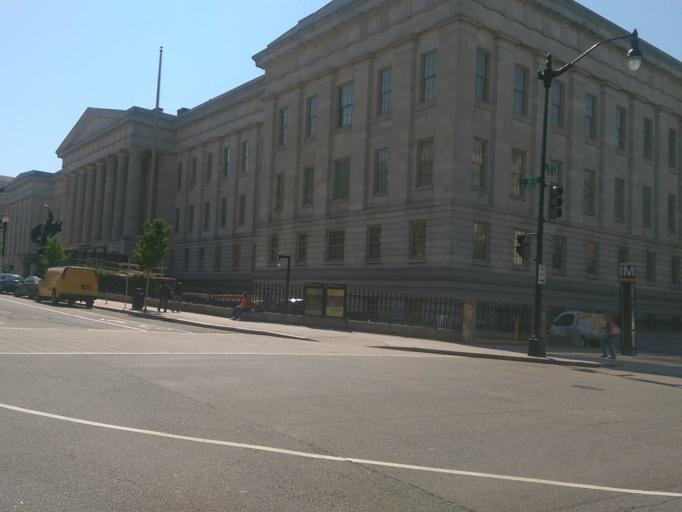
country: US
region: Washington, D.C.
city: Washington, D.C.
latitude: 38.8985
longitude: -77.0239
